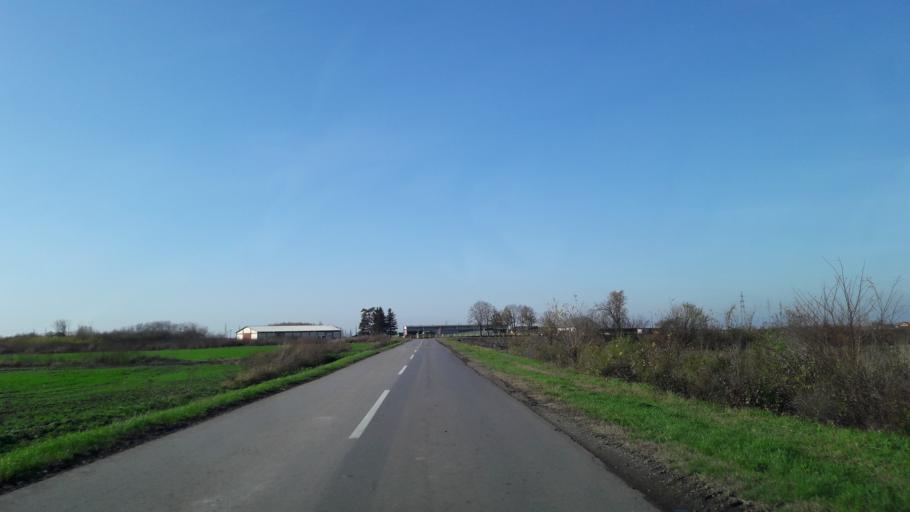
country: HR
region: Osjecko-Baranjska
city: Antunovac
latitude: 45.4758
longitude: 18.6833
